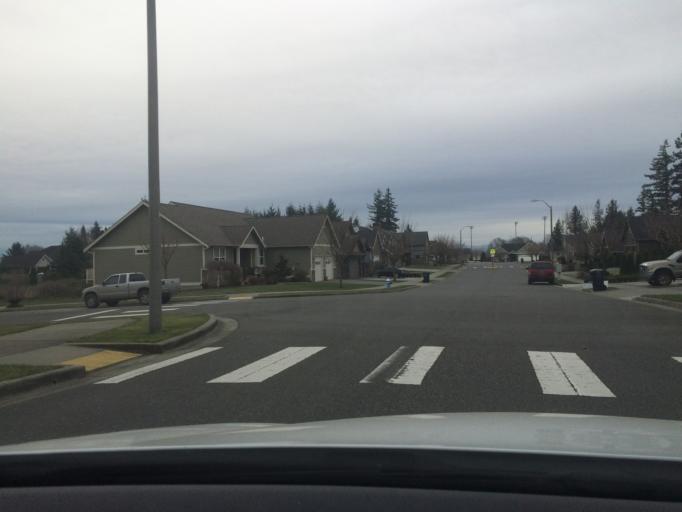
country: US
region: Washington
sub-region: Whatcom County
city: Lynden
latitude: 48.9559
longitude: -122.4252
